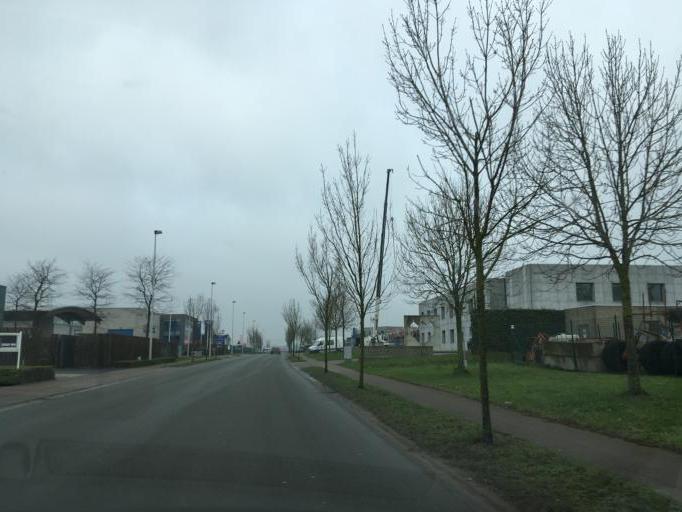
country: BE
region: Flanders
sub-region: Provincie West-Vlaanderen
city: Roeselare
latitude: 50.9516
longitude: 3.1500
